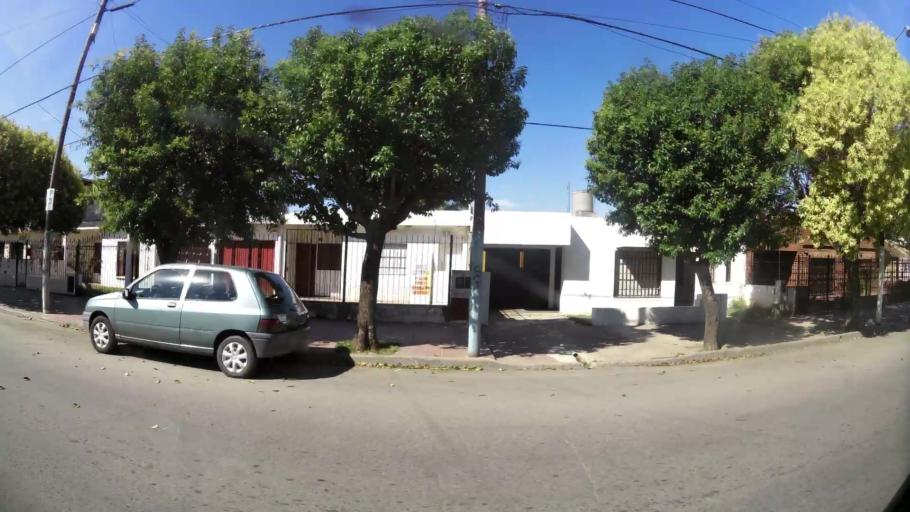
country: AR
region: Cordoba
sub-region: Departamento de Capital
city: Cordoba
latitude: -31.3626
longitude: -64.1707
